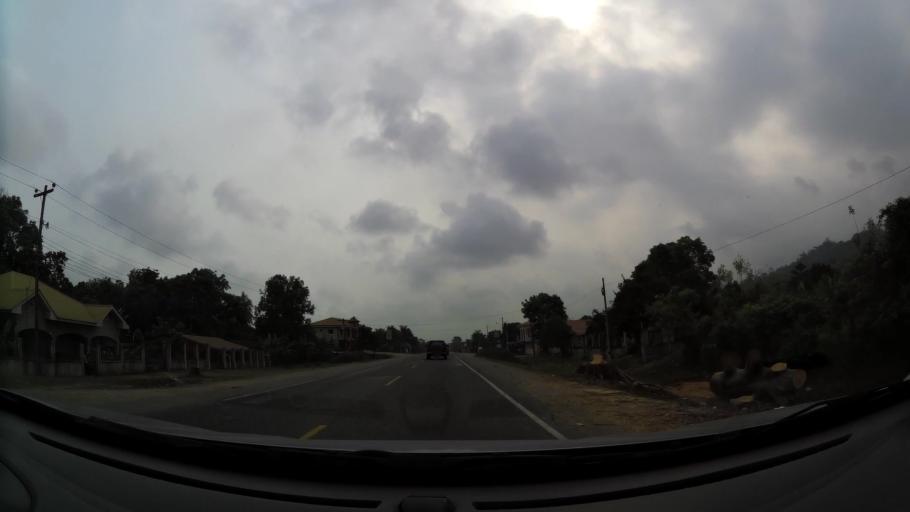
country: HN
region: Yoro
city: Guaimitas
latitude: 15.4874
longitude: -87.7595
